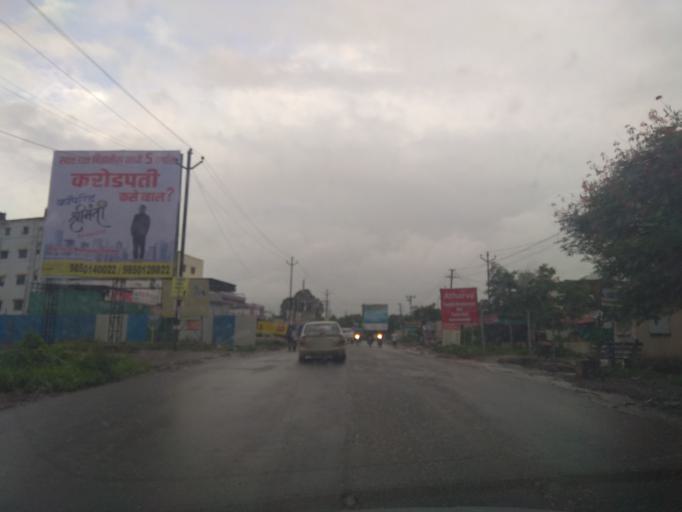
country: IN
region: Maharashtra
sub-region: Pune Division
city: Kharakvasla
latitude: 18.5112
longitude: 73.6850
